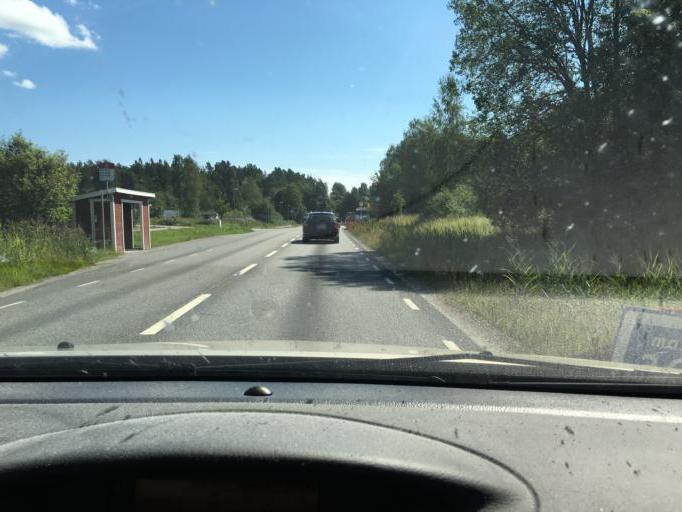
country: SE
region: Stockholm
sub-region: Varmdo Kommun
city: Mortnas
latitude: 59.2850
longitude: 18.4191
